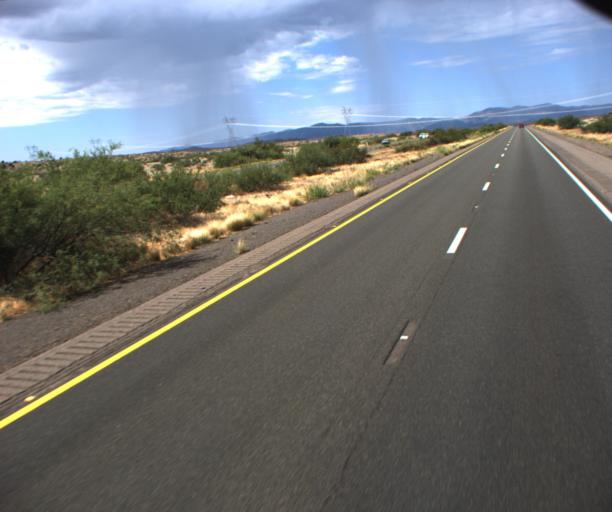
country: US
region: Arizona
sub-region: Yavapai County
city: Spring Valley
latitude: 34.3838
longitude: -112.0935
